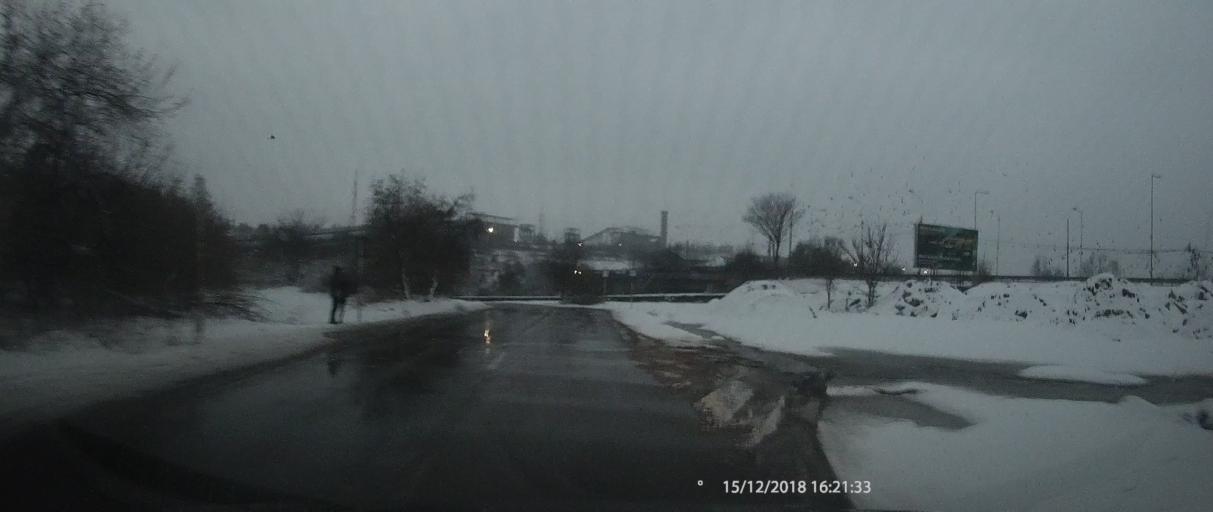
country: RO
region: Galati
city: Galati
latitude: 45.4080
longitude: 27.9984
